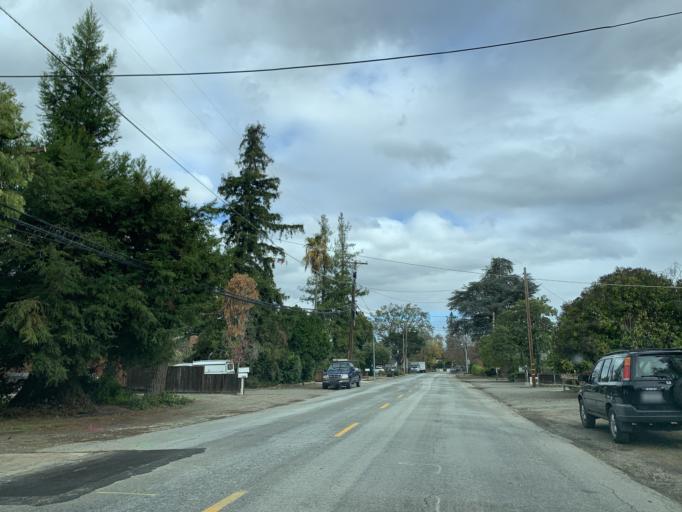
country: US
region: California
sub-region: Santa Clara County
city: Campbell
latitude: 37.2685
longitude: -121.9787
